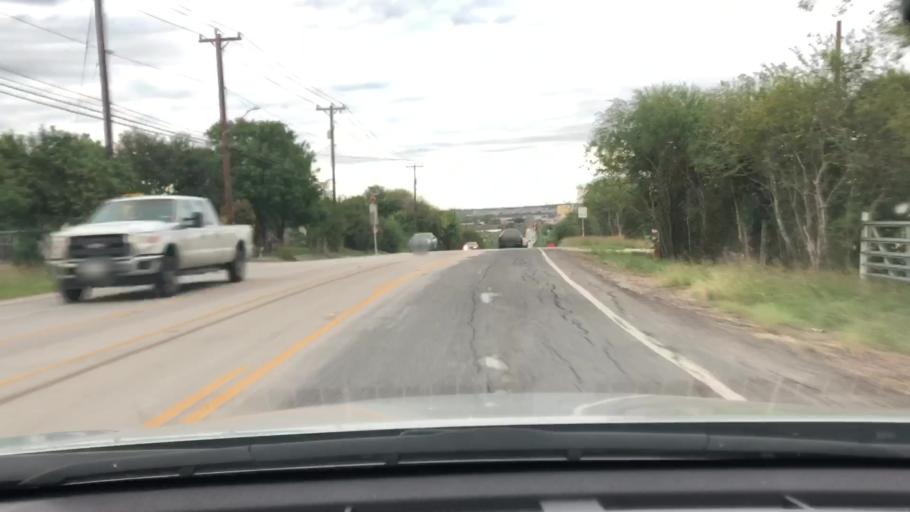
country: US
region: Texas
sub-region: Bexar County
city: Converse
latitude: 29.4938
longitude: -98.3112
